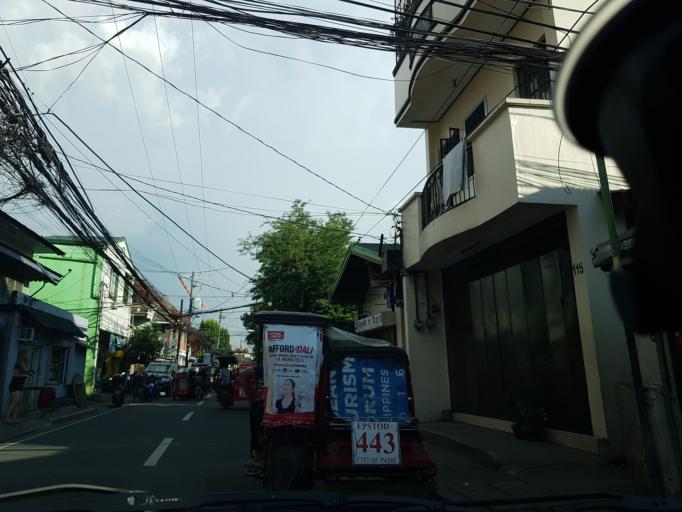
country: PH
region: Metro Manila
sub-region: Marikina
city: Calumpang
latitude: 14.6134
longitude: 121.0835
